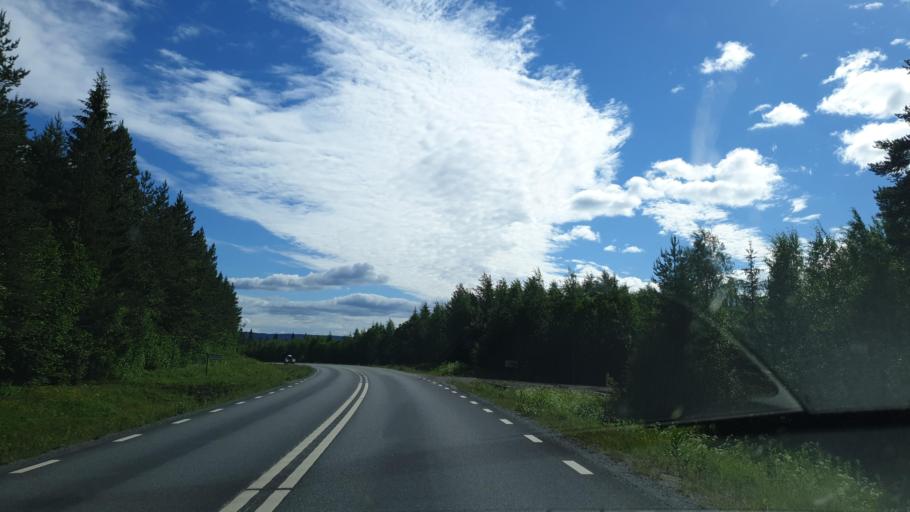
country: SE
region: Vaesterbotten
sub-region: Dorotea Kommun
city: Dorotea
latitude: 64.1421
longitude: 16.2240
